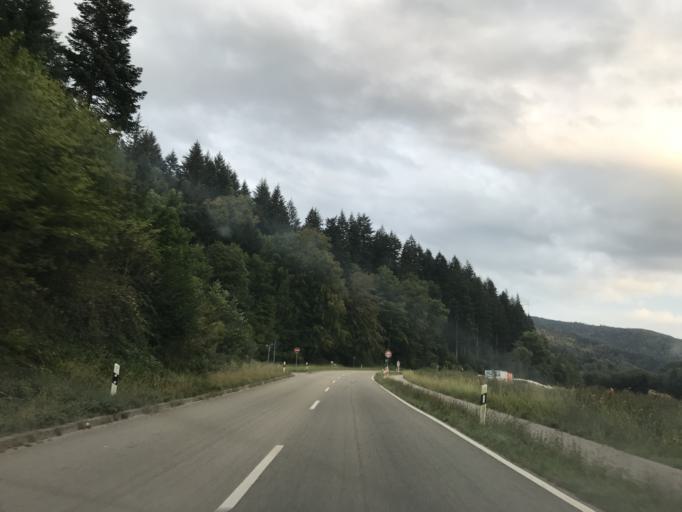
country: DE
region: Baden-Wuerttemberg
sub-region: Freiburg Region
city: Horben
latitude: 47.9490
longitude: 7.8662
